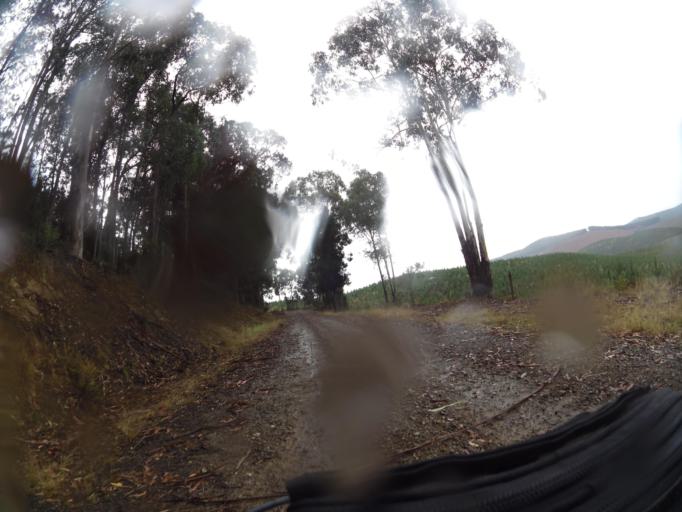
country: AU
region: New South Wales
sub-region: Greater Hume Shire
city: Holbrook
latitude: -36.2185
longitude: 147.5660
